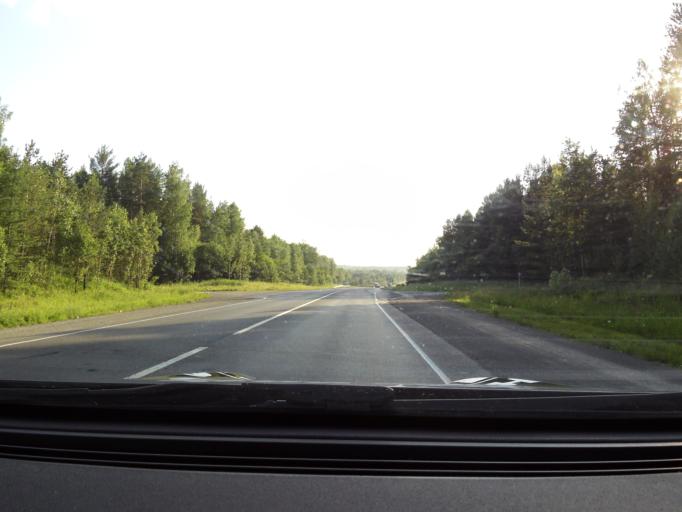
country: RU
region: Sverdlovsk
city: Druzhinino
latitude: 56.8342
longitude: 59.6360
